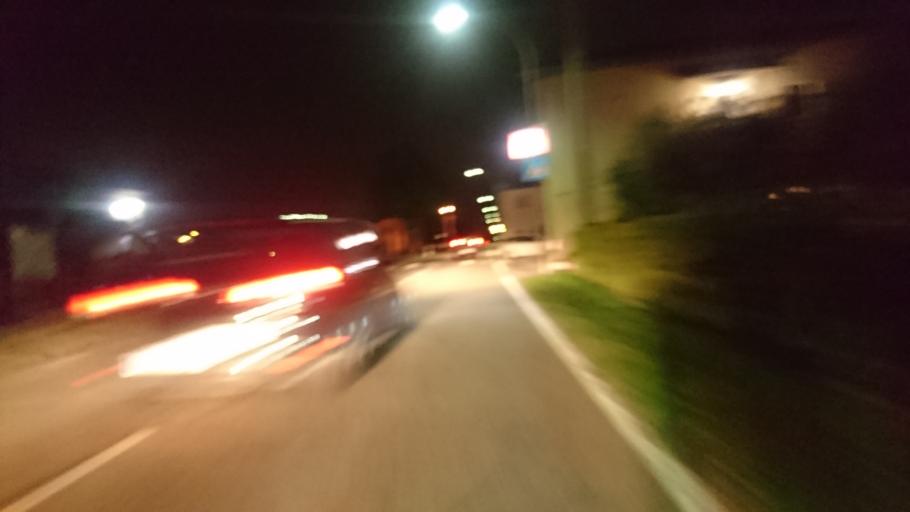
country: IT
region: Veneto
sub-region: Provincia di Treviso
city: Maser
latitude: 45.8183
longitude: 11.9880
